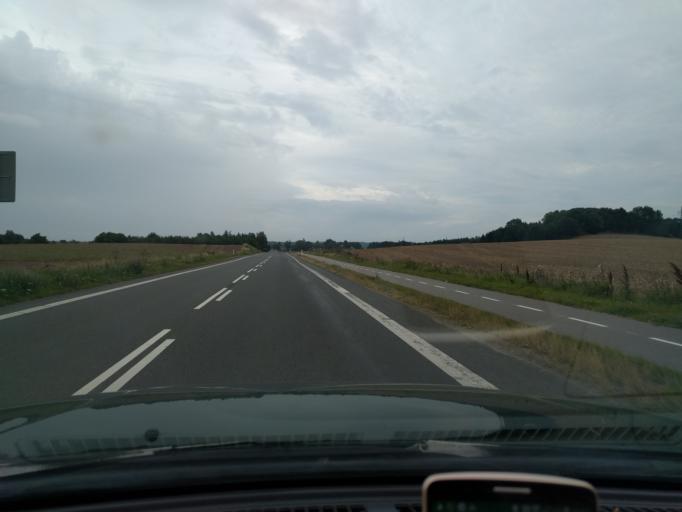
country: DK
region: Zealand
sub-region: Naestved Kommune
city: Fuglebjerg
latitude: 55.2376
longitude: 11.4333
